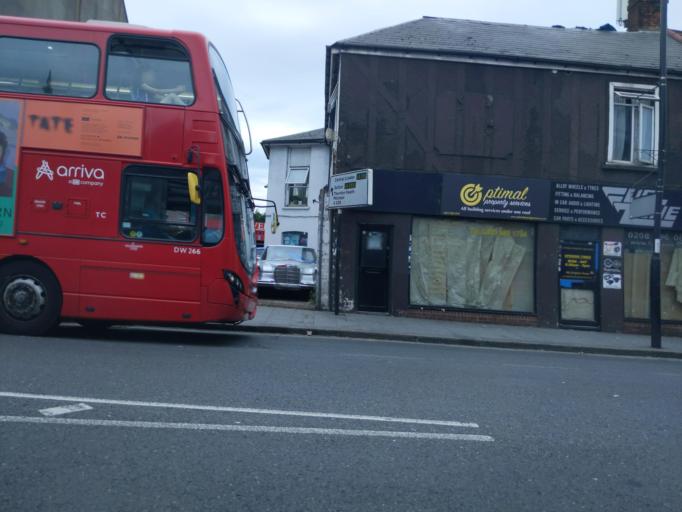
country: GB
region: England
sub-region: Greater London
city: South Croydon
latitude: 51.3644
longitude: -0.0988
